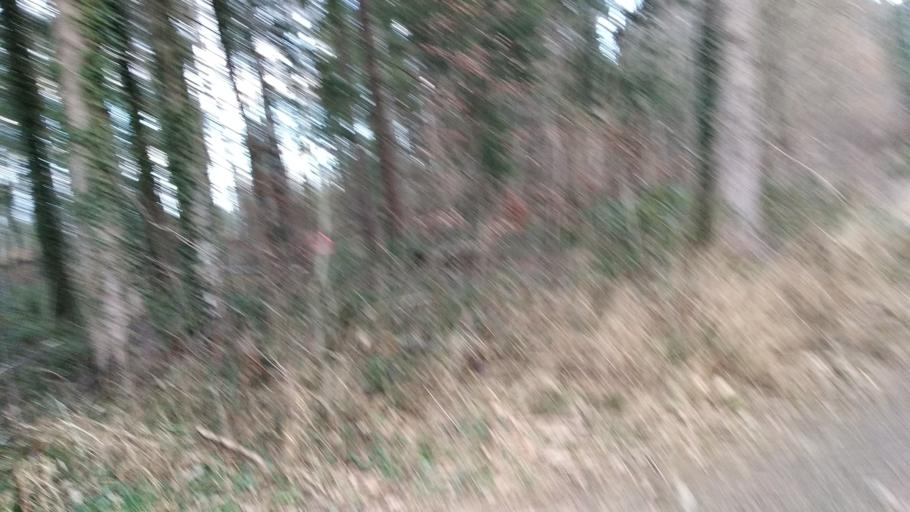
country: DE
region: Bavaria
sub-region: Upper Bavaria
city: Ottobrunn
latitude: 48.0771
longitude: 11.6855
